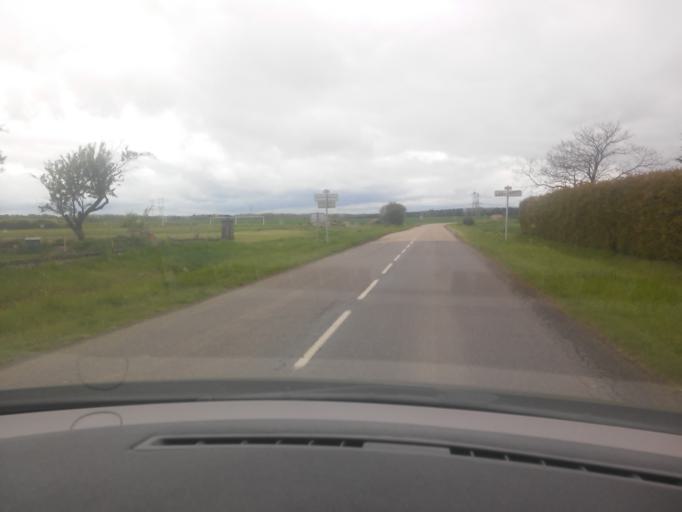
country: FR
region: Lorraine
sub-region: Departement de la Moselle
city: Mecleuves
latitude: 49.0813
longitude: 6.3069
